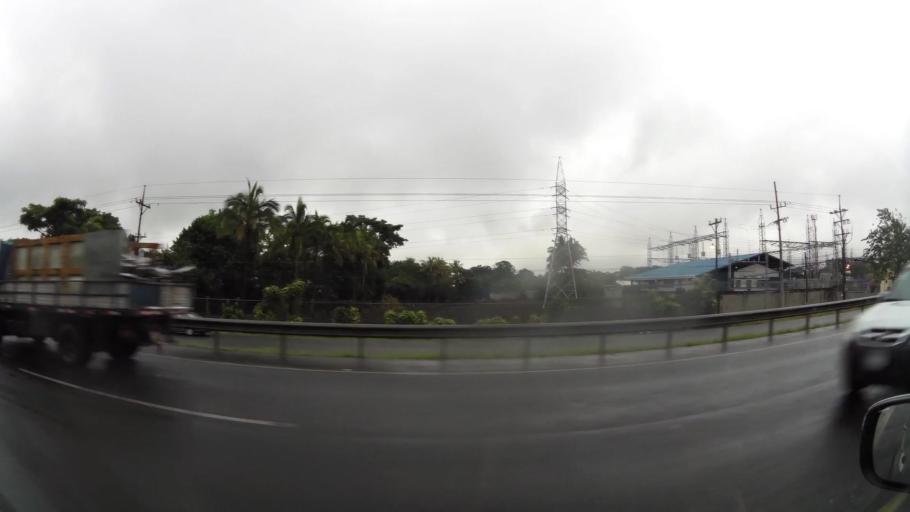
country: CR
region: Alajuela
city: Alajuela
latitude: 9.9972
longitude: -84.2257
